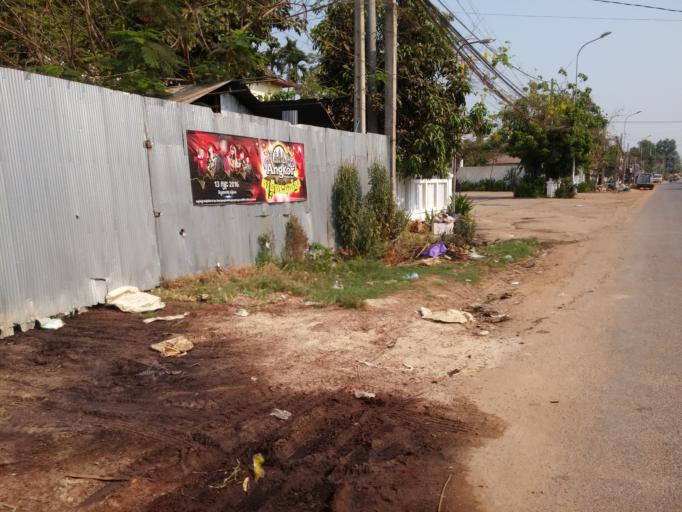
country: KH
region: Siem Reap
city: Siem Reap
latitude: 13.3716
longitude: 103.8496
